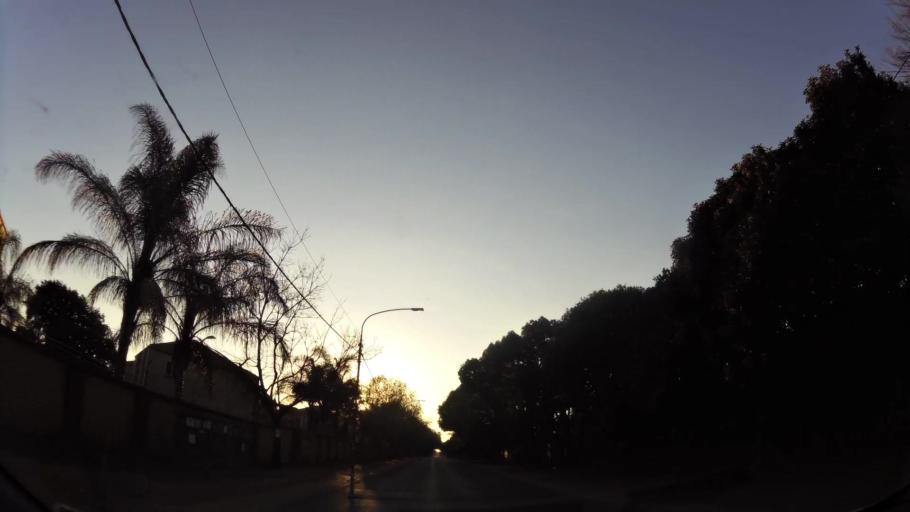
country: ZA
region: Gauteng
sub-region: City of Tshwane Metropolitan Municipality
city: Centurion
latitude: -25.8560
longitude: 28.1998
